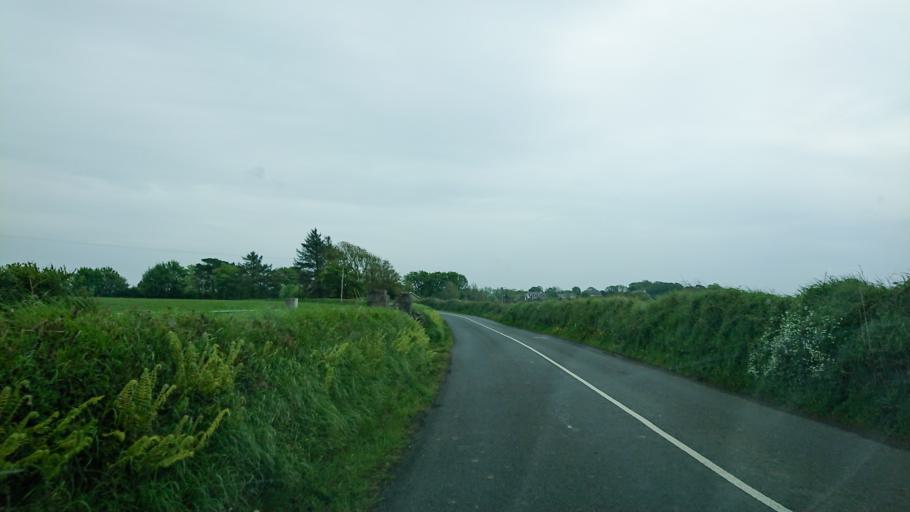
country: IE
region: Munster
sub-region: Waterford
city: Waterford
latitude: 52.2184
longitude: -7.0463
